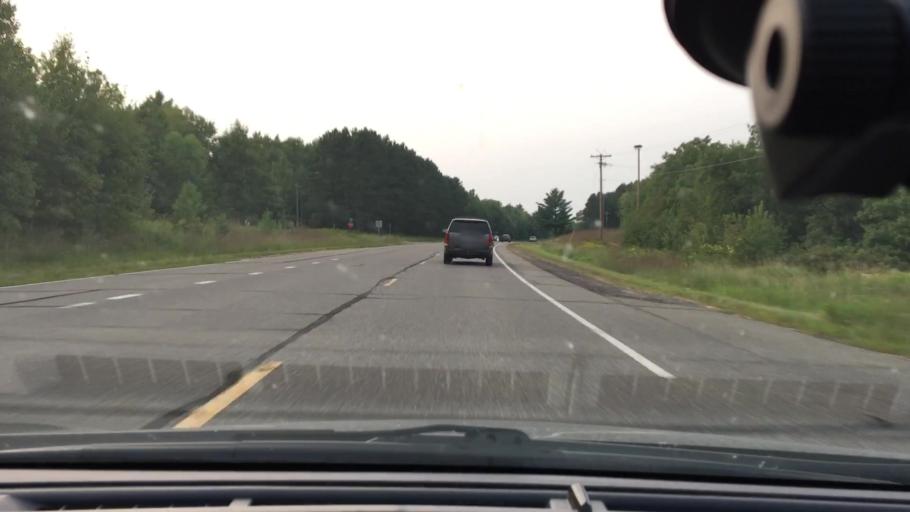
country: US
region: Minnesota
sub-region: Crow Wing County
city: Crosby
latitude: 46.4588
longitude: -93.8838
